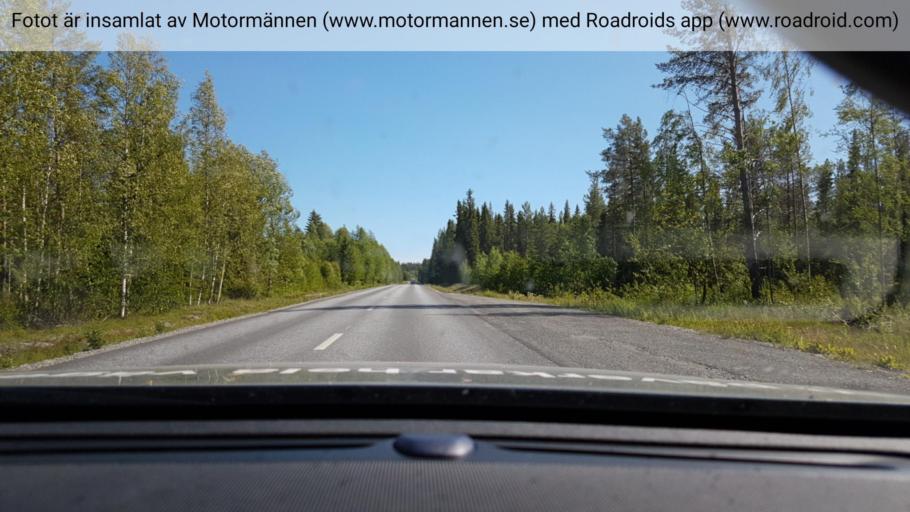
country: SE
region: Vaesterbotten
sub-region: Vilhelmina Kommun
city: Sjoberg
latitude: 64.7099
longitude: 16.2474
